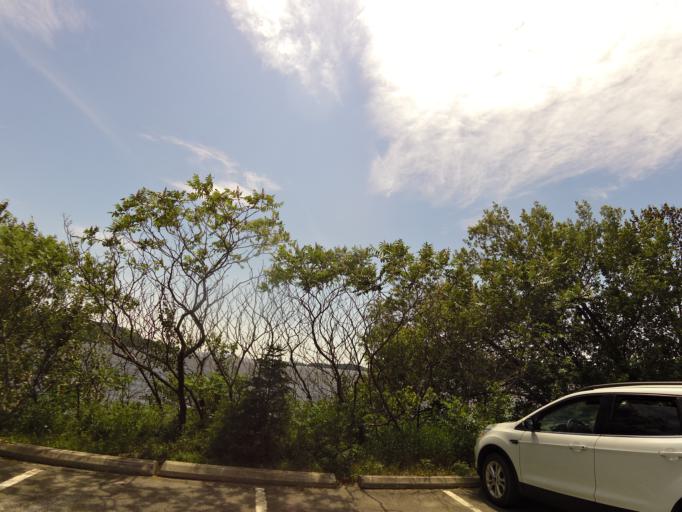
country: CA
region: Quebec
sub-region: Abitibi-Temiscamingue
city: Ville-Marie
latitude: 47.2903
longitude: -79.4555
